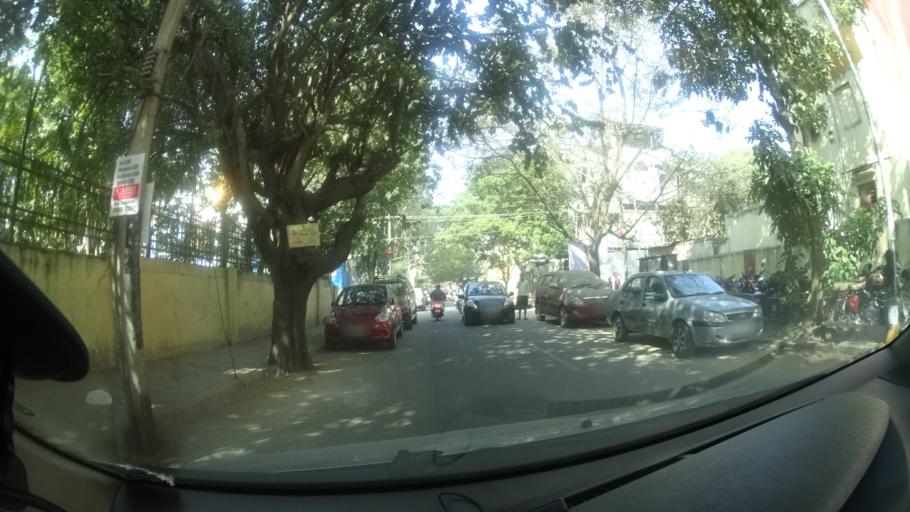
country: IN
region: Karnataka
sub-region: Bangalore Urban
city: Bangalore
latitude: 13.0062
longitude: 77.5755
